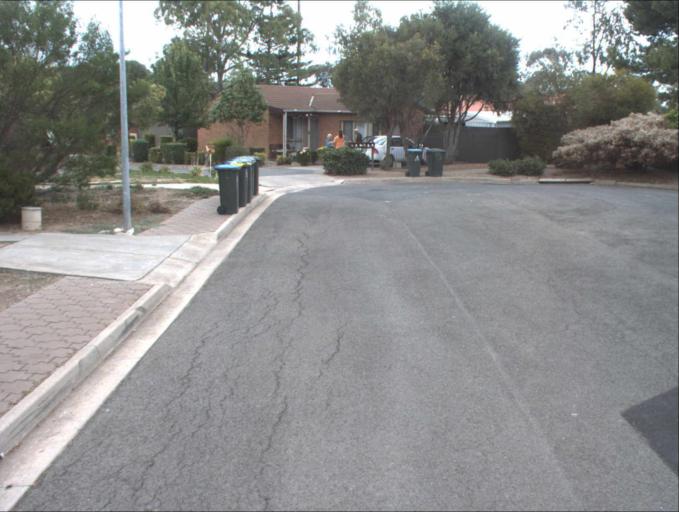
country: AU
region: South Australia
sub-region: Port Adelaide Enfield
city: Gilles Plains
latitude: -34.8495
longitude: 138.6543
